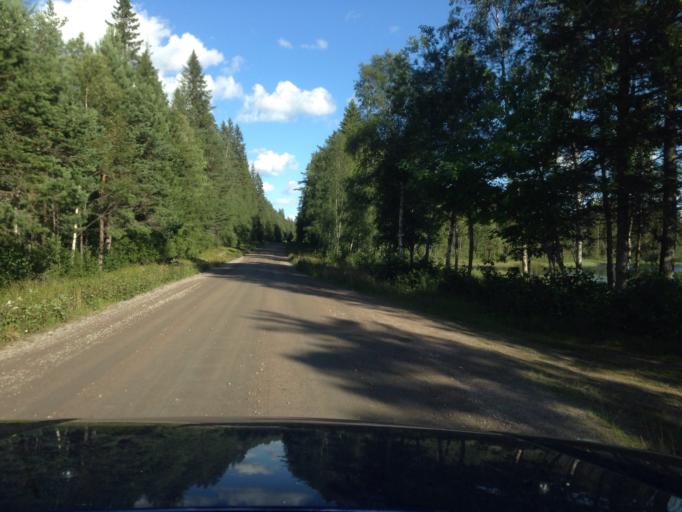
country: SE
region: Dalarna
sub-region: Ludvika Kommun
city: Abborrberget
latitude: 60.2556
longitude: 14.7503
